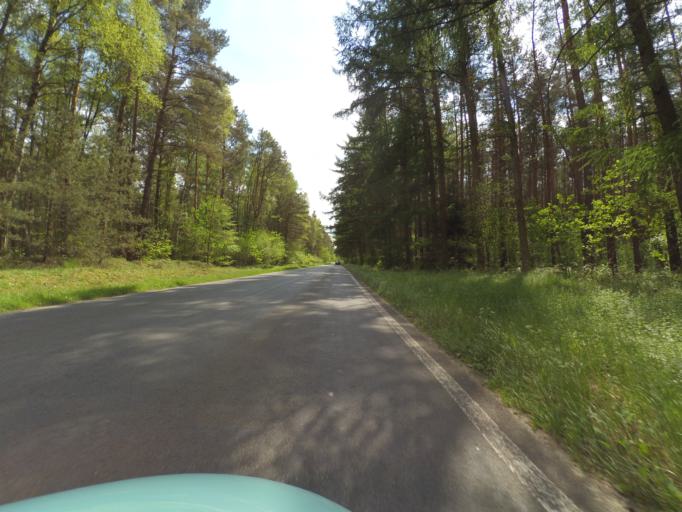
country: DE
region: Lower Saxony
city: Hambuhren
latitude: 52.6119
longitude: 9.9829
